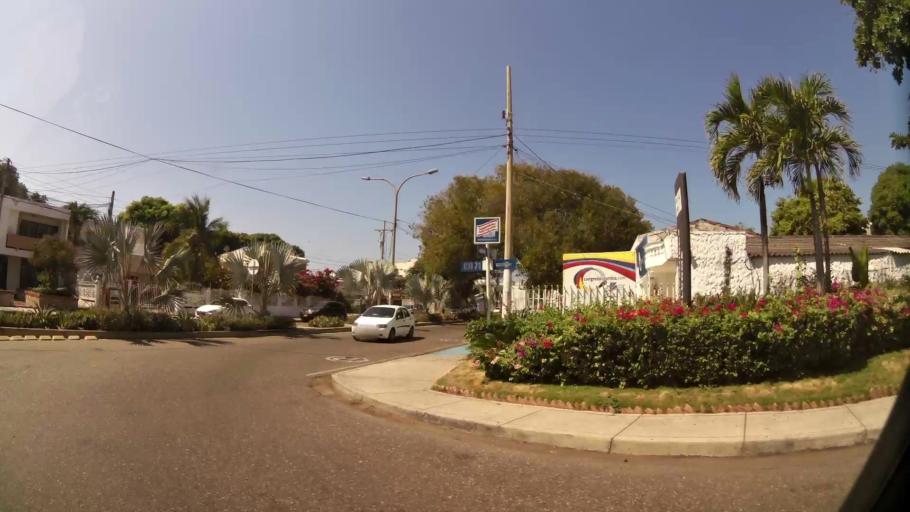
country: CO
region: Bolivar
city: Cartagena
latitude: 10.4446
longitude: -75.5168
